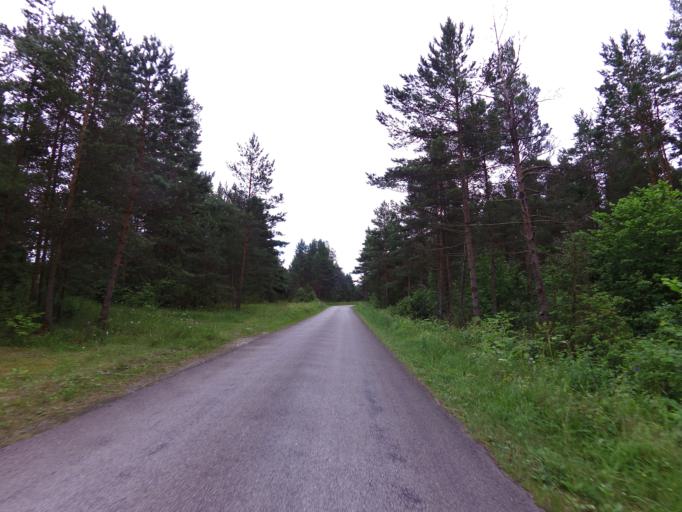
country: EE
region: Laeaene
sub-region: Vormsi vald
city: Hullo
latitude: 58.9778
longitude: 23.2558
